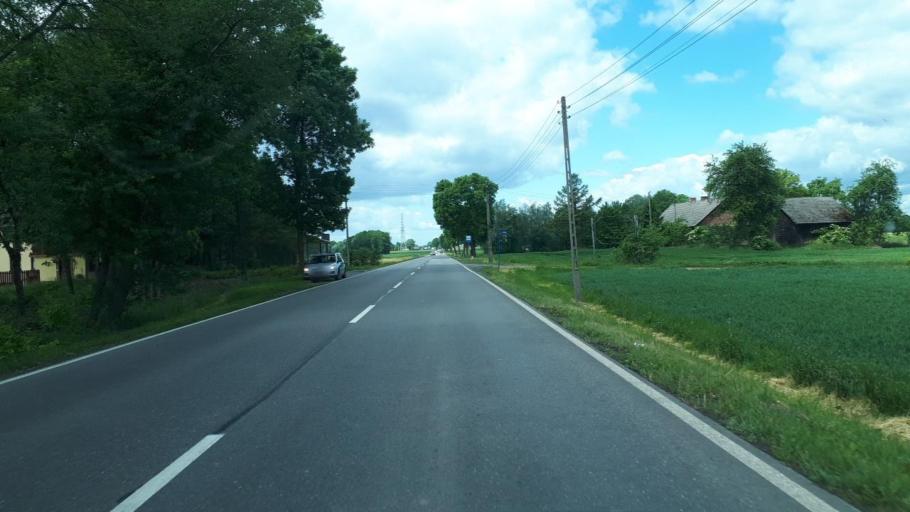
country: PL
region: Silesian Voivodeship
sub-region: Powiat pszczynski
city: Frydek
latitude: 49.9704
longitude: 19.0759
